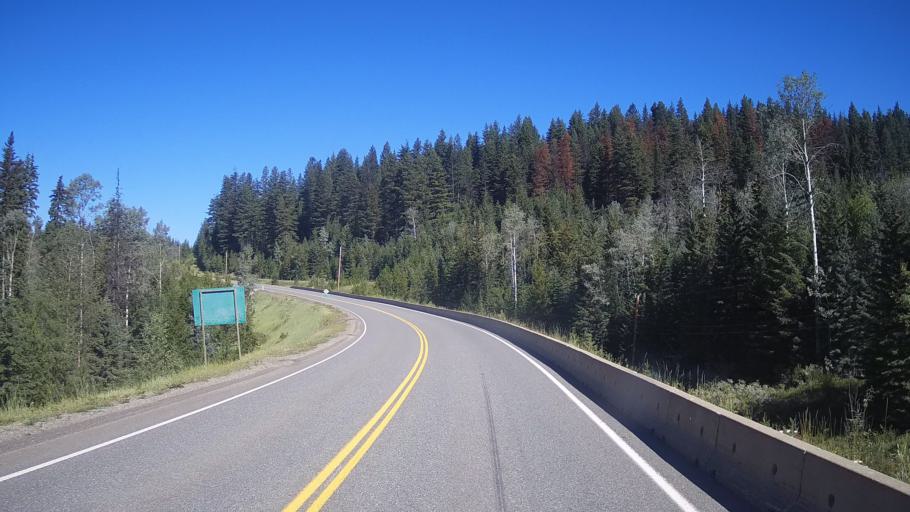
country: CA
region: British Columbia
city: Kamloops
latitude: 51.4749
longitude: -120.5561
